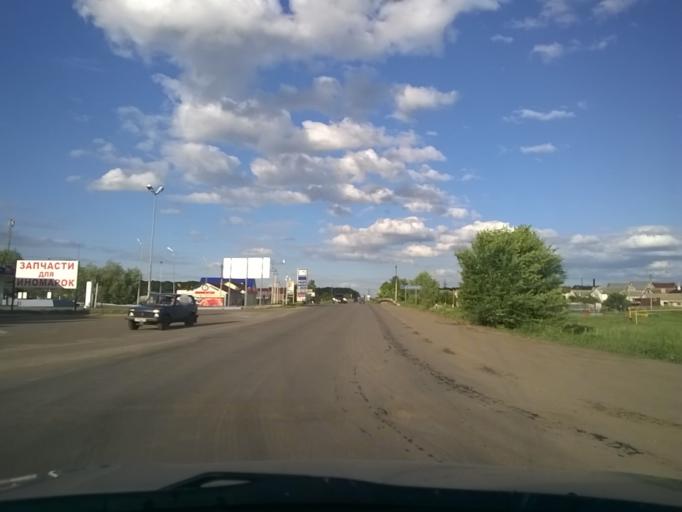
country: RU
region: Volgograd
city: Uryupinsk
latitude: 50.8213
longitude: 42.0440
